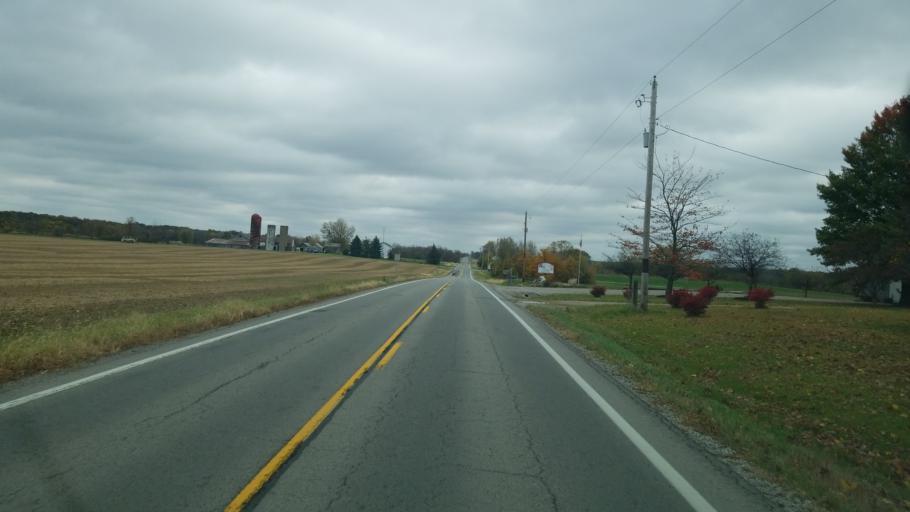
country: US
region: Ohio
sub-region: Seneca County
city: Tiffin
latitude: 41.0812
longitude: -83.0000
